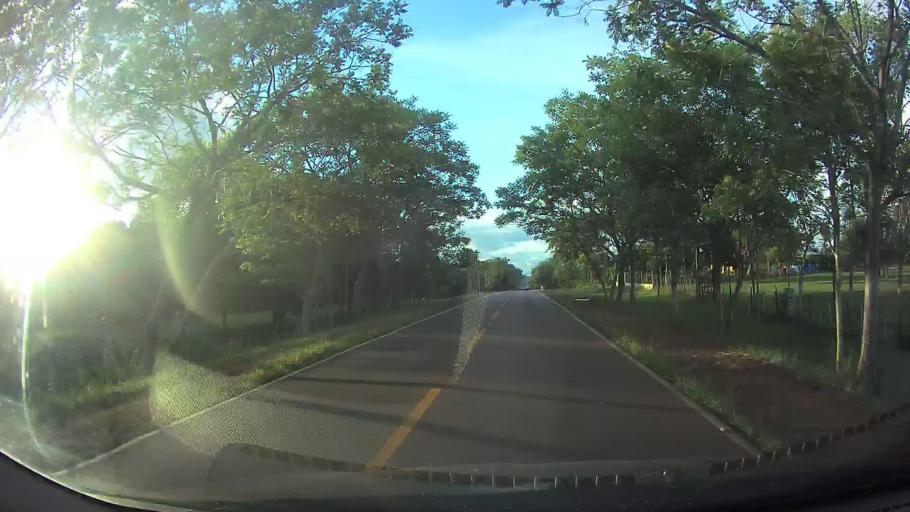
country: PY
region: Paraguari
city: Carapegua
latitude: -25.7951
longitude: -57.2036
